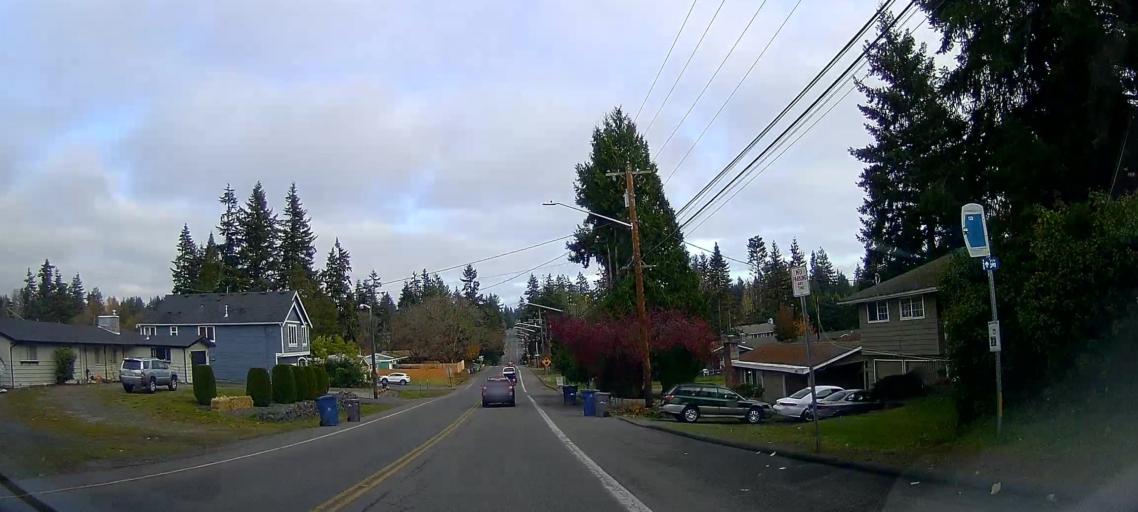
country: US
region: Washington
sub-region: Snohomish County
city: Alderwood Manor
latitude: 47.8136
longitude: -122.2734
